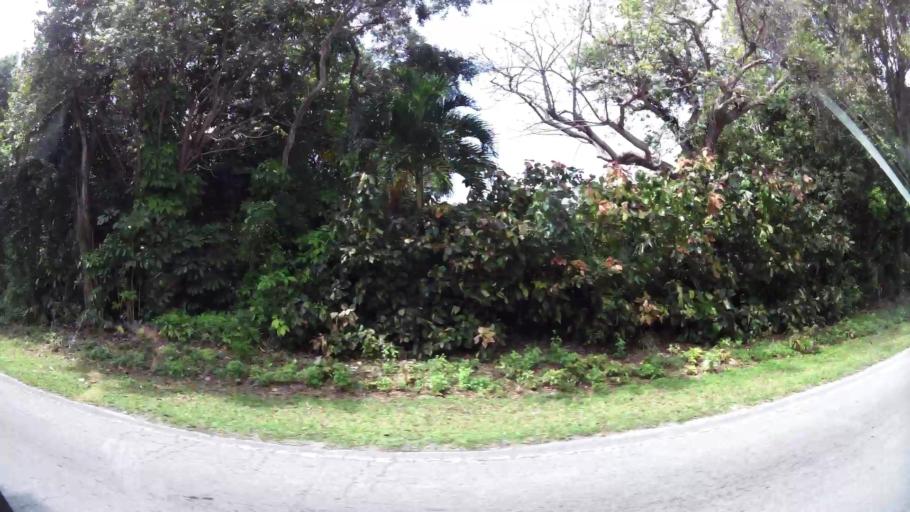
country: BS
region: Freeport
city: Lucaya
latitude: 26.5199
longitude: -78.6497
